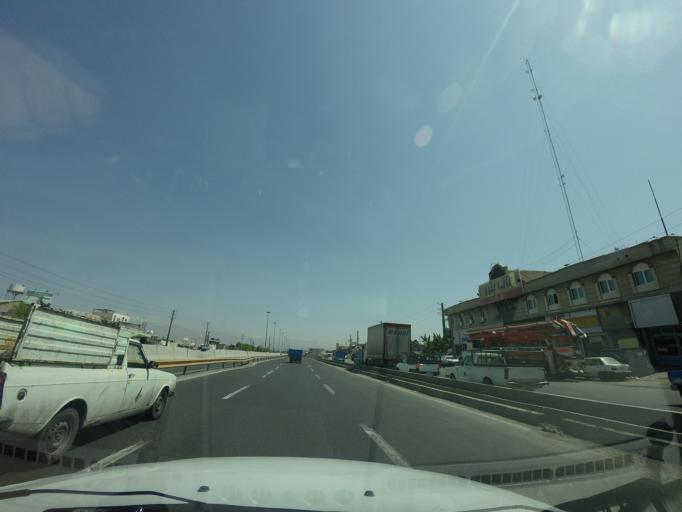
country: IR
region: Tehran
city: Rey
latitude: 35.6240
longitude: 51.3304
